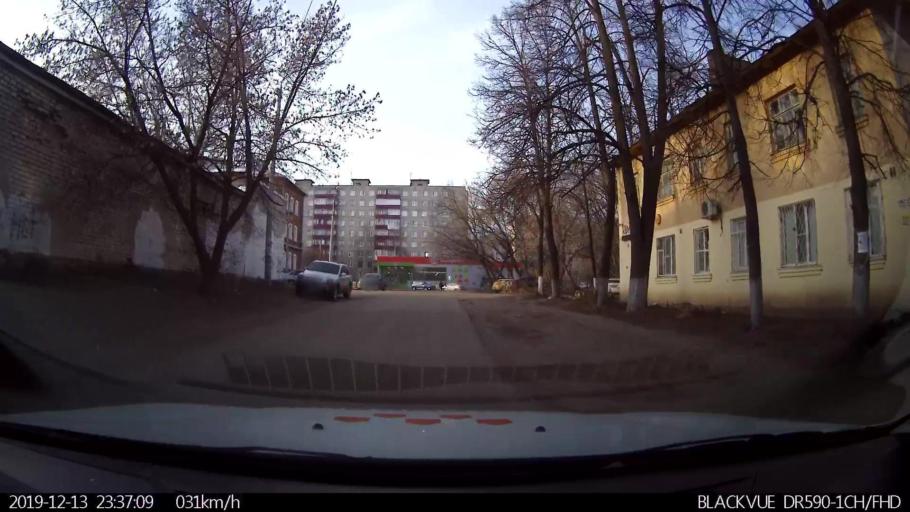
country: RU
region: Nizjnij Novgorod
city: Nizhniy Novgorod
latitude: 56.2932
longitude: 43.9434
